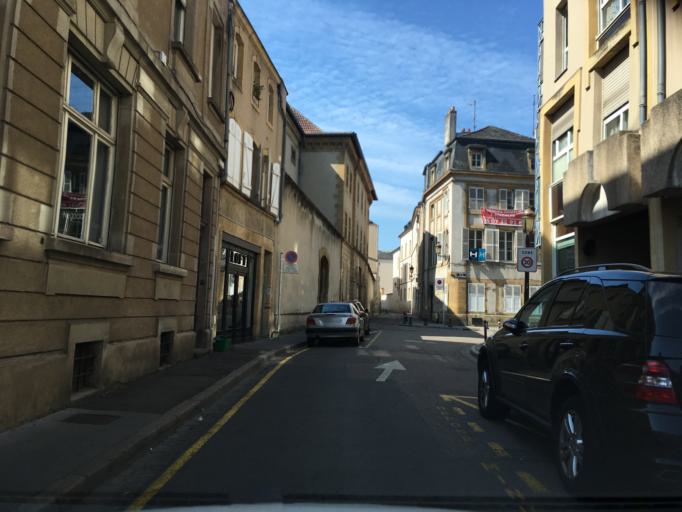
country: FR
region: Lorraine
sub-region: Departement de la Moselle
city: Metz
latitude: 49.1146
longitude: 6.1757
